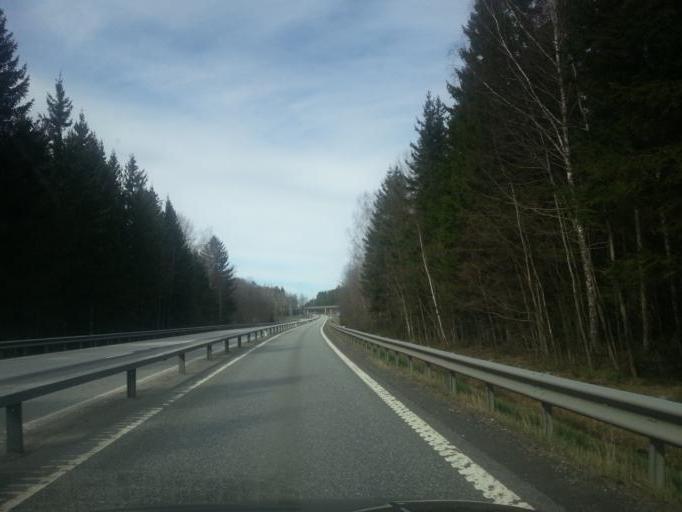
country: SE
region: Joenkoeping
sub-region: Jonkopings Kommun
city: Bankeryd
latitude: 57.8496
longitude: 14.1047
